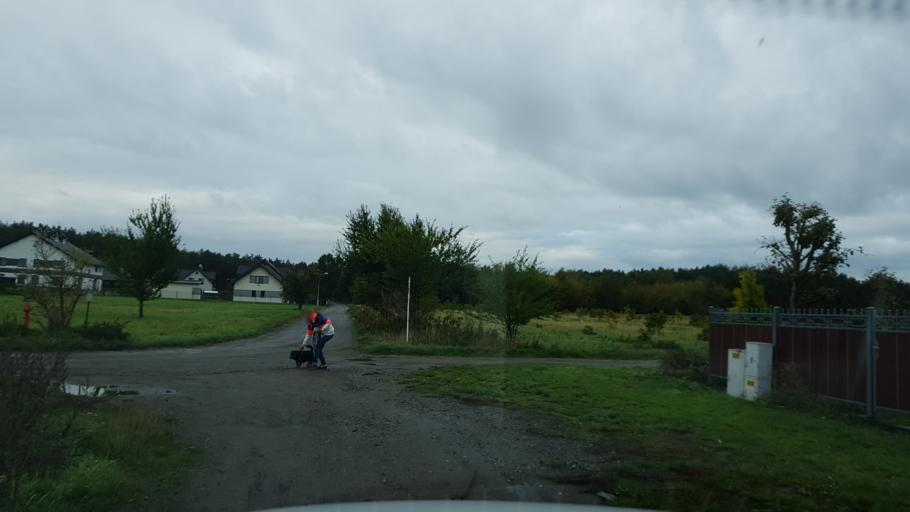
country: PL
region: West Pomeranian Voivodeship
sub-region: Powiat kamienski
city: Wolin
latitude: 53.8369
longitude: 14.6052
